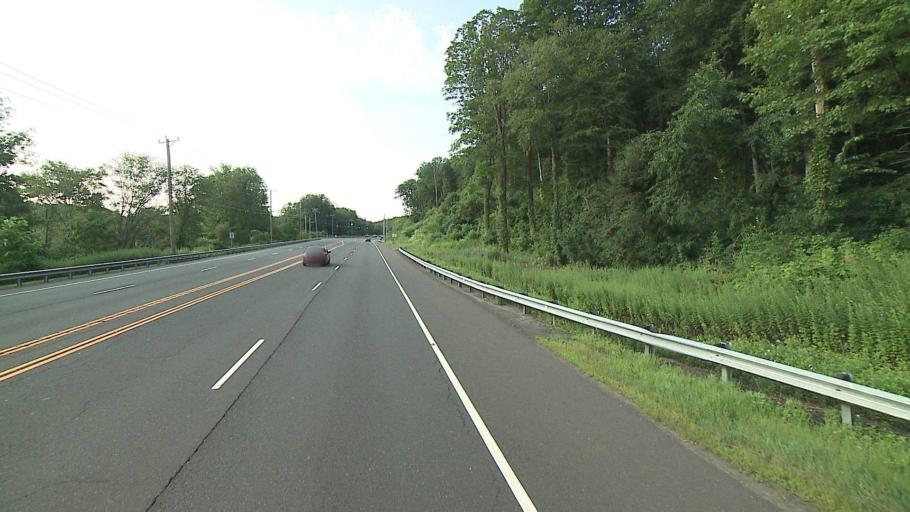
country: US
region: Connecticut
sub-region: Fairfield County
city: Danbury
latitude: 41.3486
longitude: -73.4693
